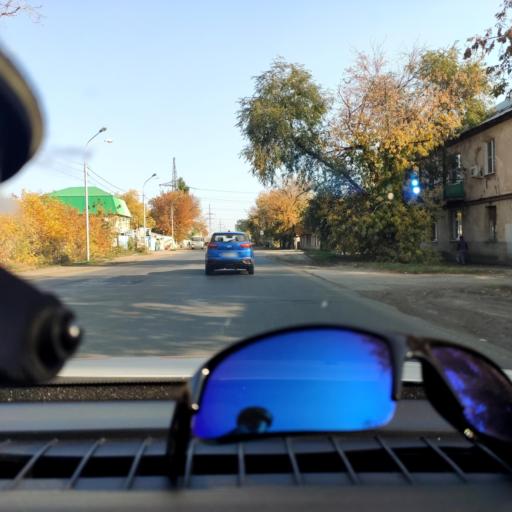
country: RU
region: Samara
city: Samara
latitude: 53.1338
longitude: 50.1221
